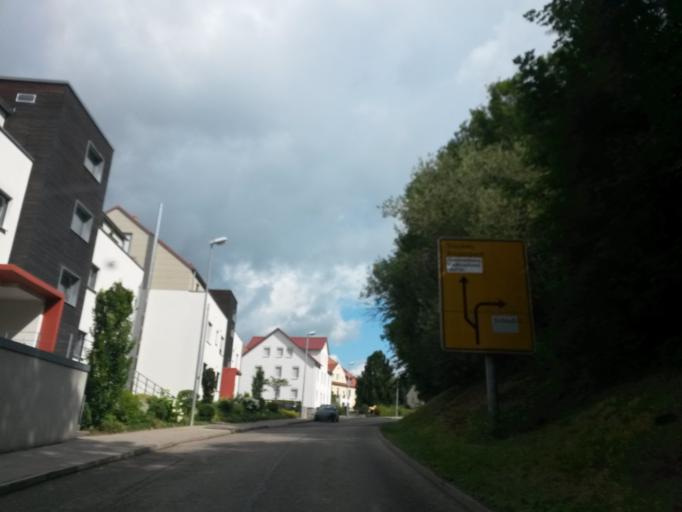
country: DE
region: Baden-Wuerttemberg
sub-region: Regierungsbezirk Stuttgart
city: Ellwangen
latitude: 48.9634
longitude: 10.1349
